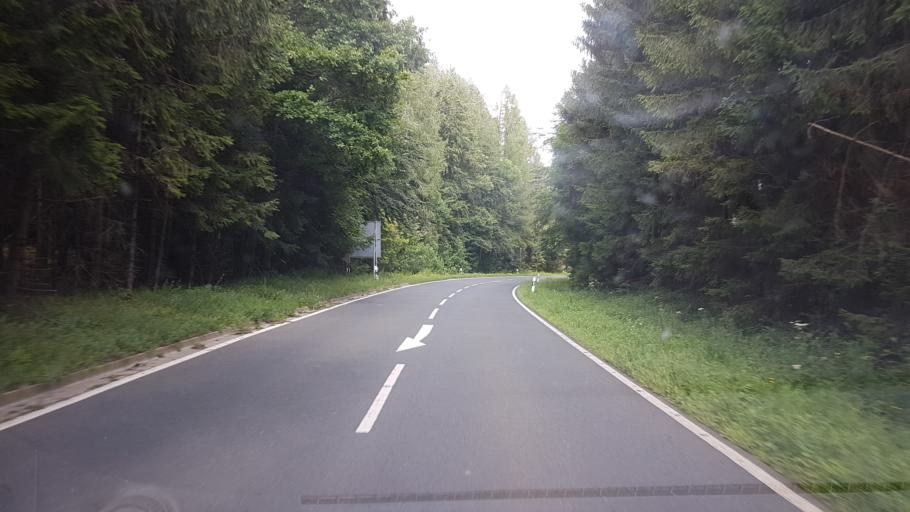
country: DE
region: Bavaria
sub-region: Upper Franconia
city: Gossweinstein
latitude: 49.7637
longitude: 11.2746
